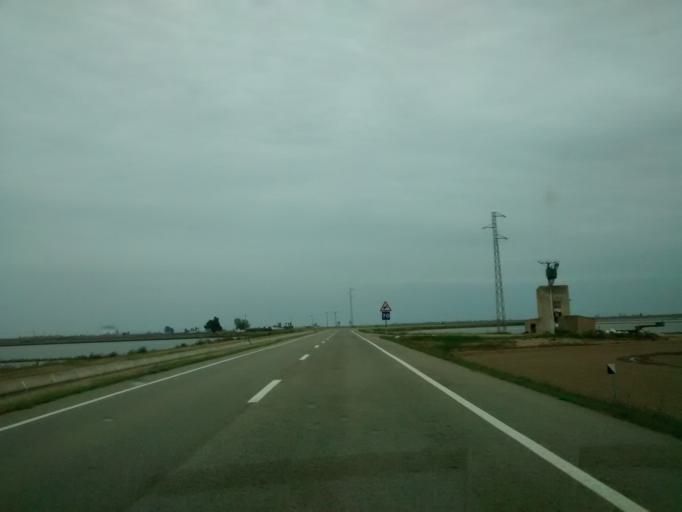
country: ES
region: Catalonia
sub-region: Provincia de Tarragona
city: Deltebre
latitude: 40.6952
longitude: 0.6811
